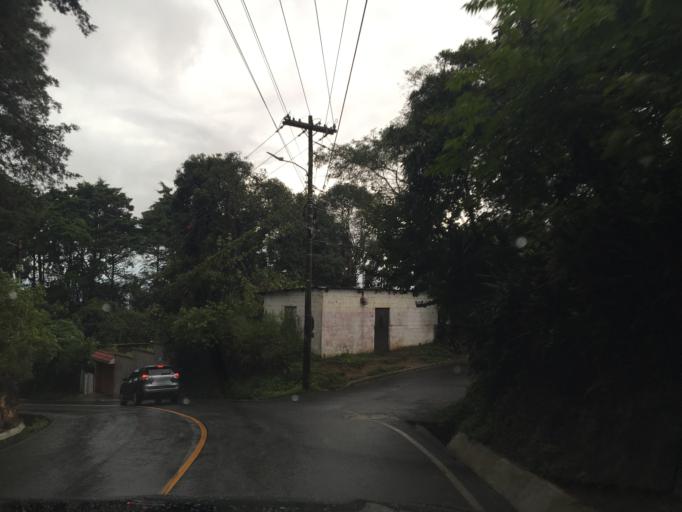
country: GT
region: Guatemala
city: Santa Catarina Pinula
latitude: 14.5573
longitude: -90.5033
